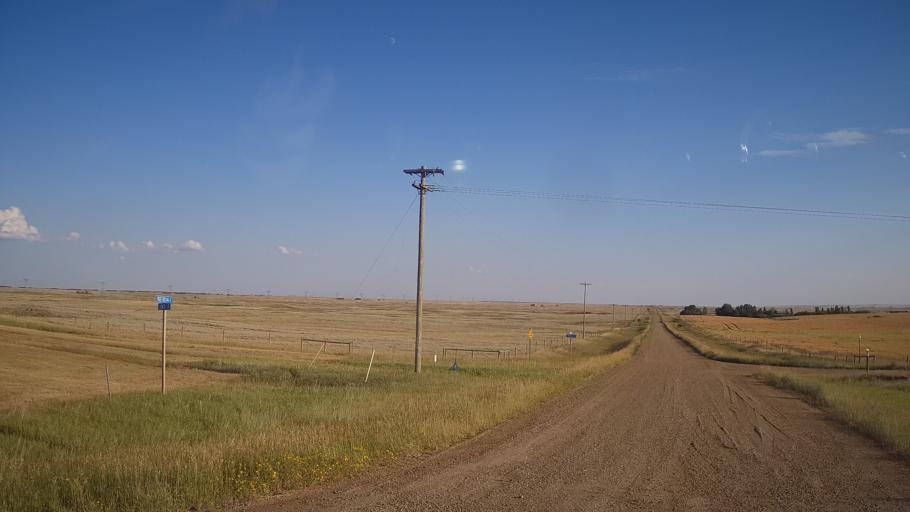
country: CA
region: Alberta
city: Hanna
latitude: 51.6203
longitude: -111.8570
